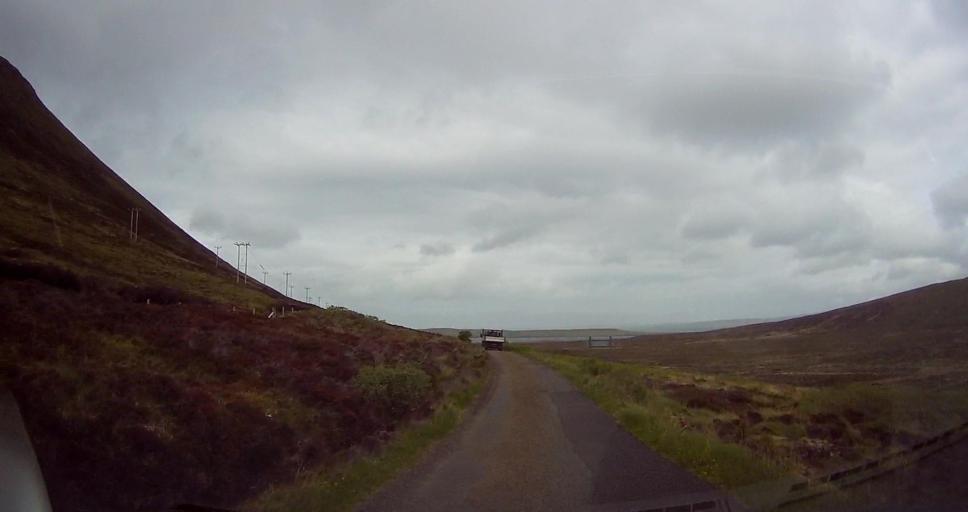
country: GB
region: Scotland
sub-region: Orkney Islands
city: Stromness
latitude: 58.8892
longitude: -3.3158
